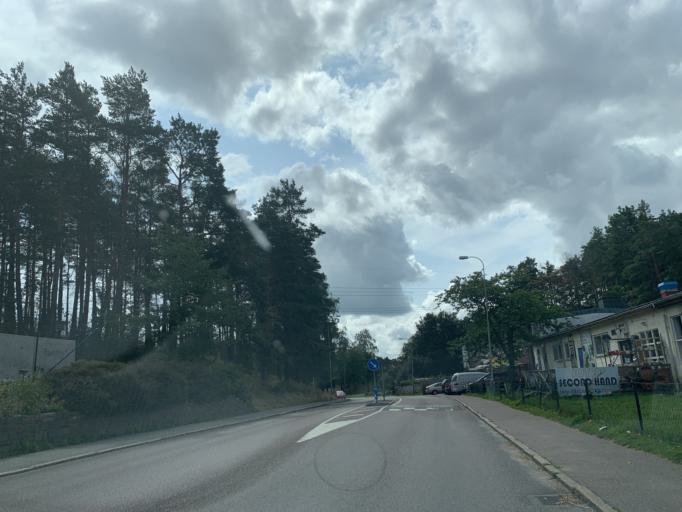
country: SE
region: Vaestra Goetaland
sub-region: Goteborg
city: Eriksbo
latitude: 57.7597
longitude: 12.0418
